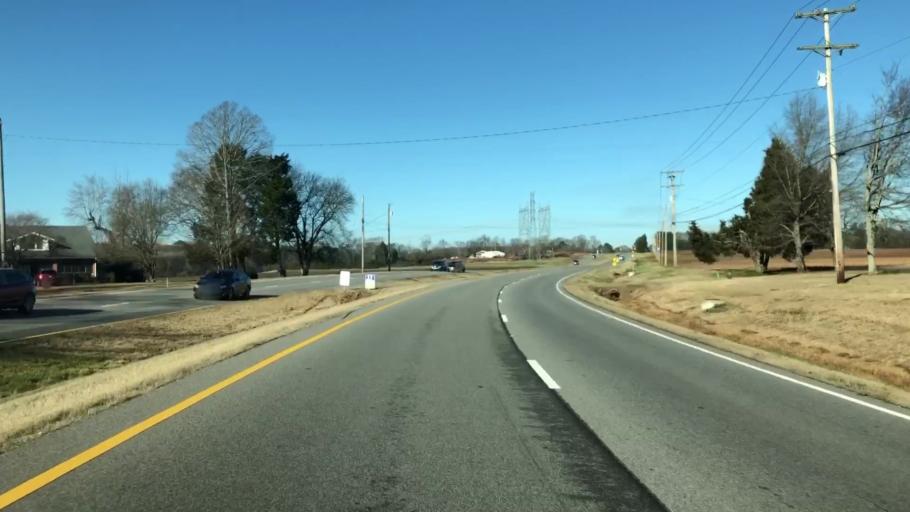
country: US
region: Alabama
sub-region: Madison County
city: Madison
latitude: 34.7527
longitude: -86.8256
